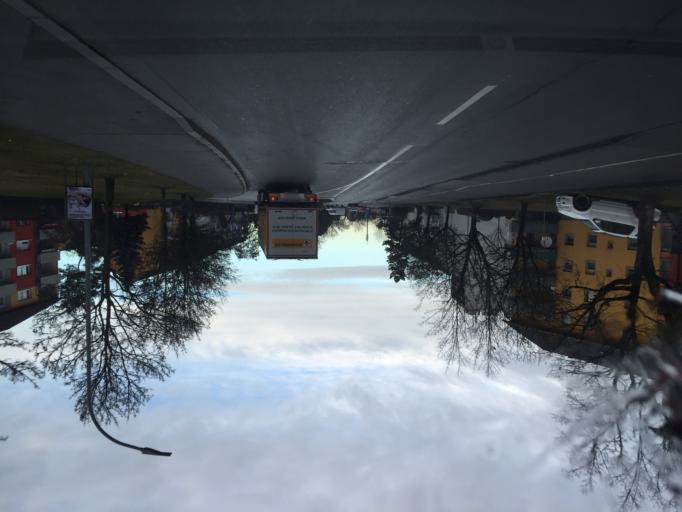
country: DE
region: Baden-Wuerttemberg
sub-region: Freiburg Region
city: Rielasingen-Worblingen
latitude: 47.7413
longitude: 8.8507
